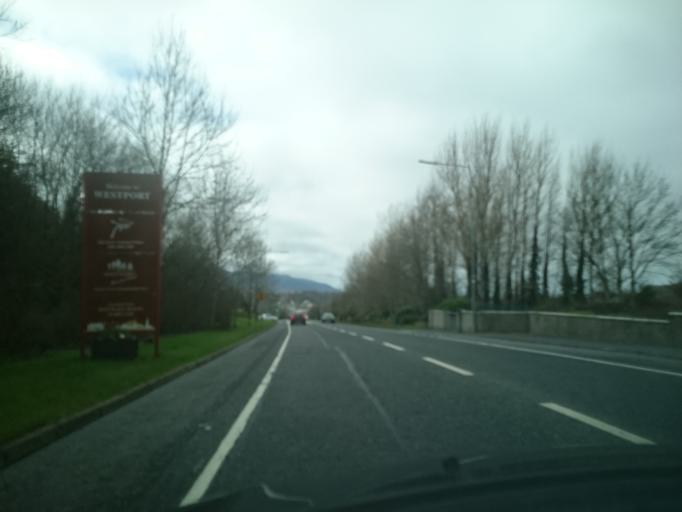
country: IE
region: Connaught
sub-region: Maigh Eo
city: Westport
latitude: 53.8036
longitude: -9.5081
